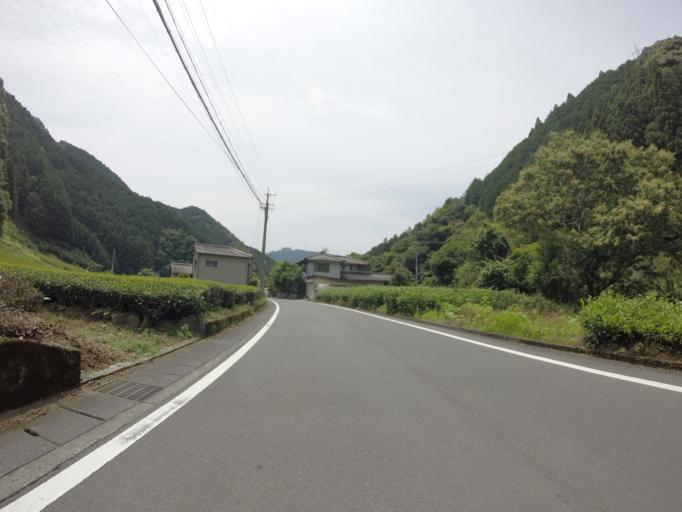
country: JP
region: Shizuoka
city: Shizuoka-shi
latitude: 35.0236
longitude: 138.2866
